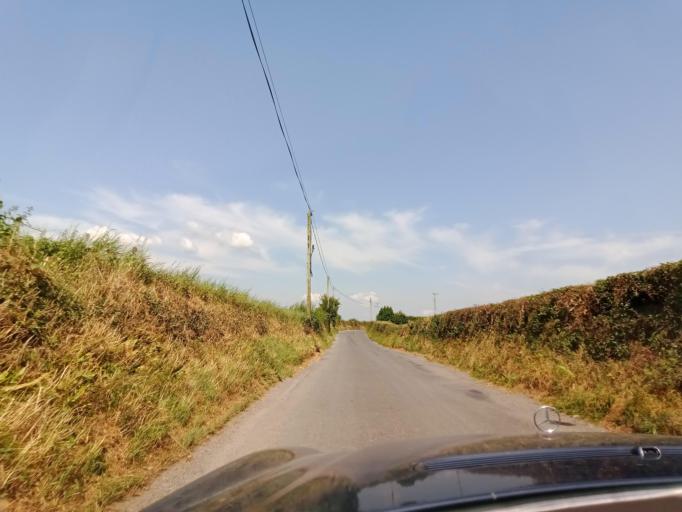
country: IE
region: Leinster
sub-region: Kilkenny
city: Mooncoin
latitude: 52.2873
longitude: -7.2343
